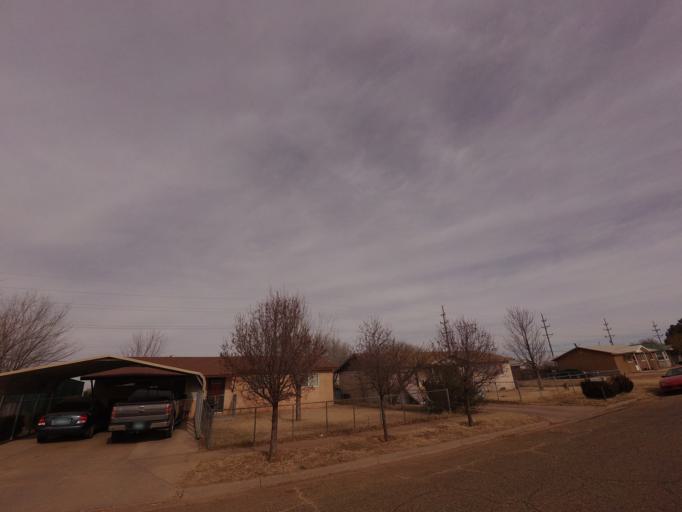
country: US
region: New Mexico
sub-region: Curry County
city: Clovis
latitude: 34.4115
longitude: -103.2443
